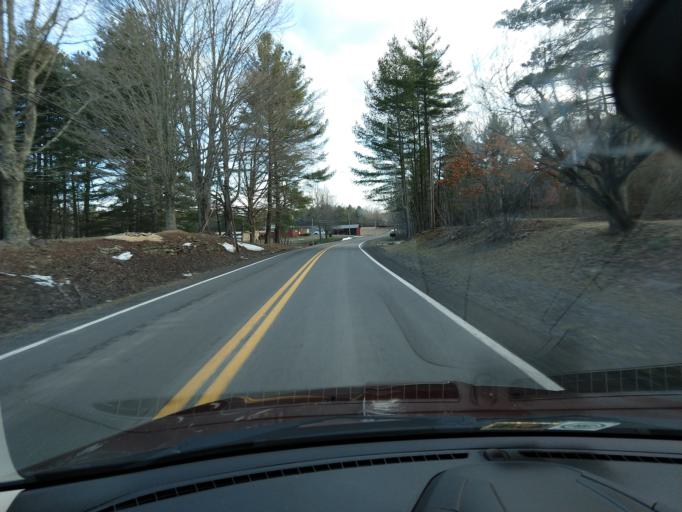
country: US
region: West Virginia
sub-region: Pocahontas County
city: Marlinton
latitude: 38.0734
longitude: -80.2874
